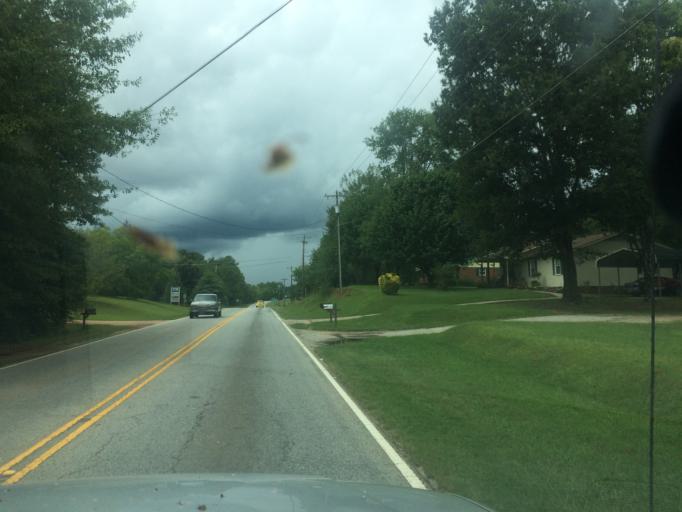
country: US
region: South Carolina
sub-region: Greenville County
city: Taylors
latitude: 34.9705
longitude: -82.3250
